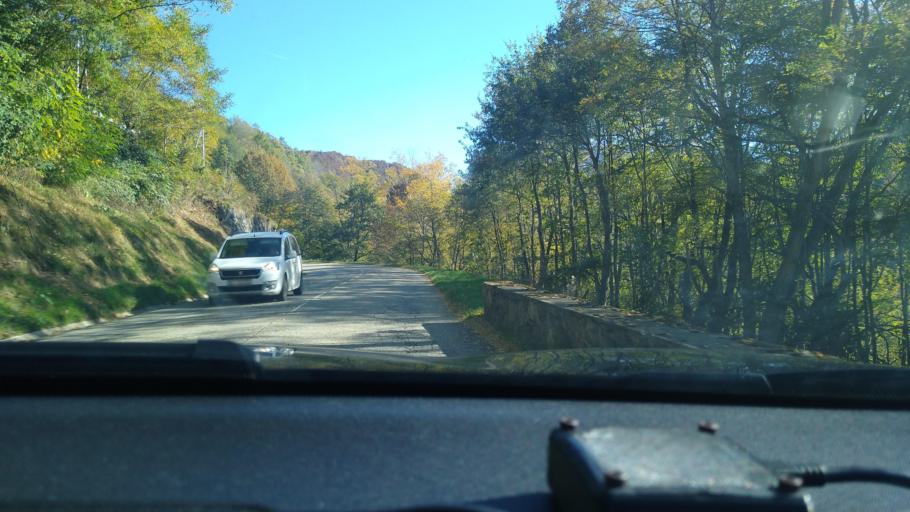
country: FR
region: Midi-Pyrenees
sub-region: Departement de l'Ariege
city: Ax-les-Thermes
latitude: 42.7229
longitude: 1.8569
